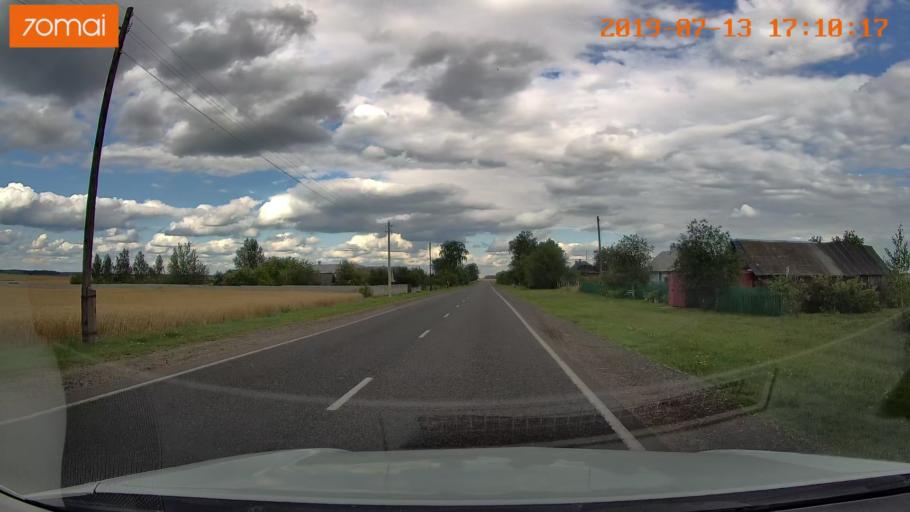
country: BY
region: Mogilev
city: Babruysk
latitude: 53.2691
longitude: 29.2776
